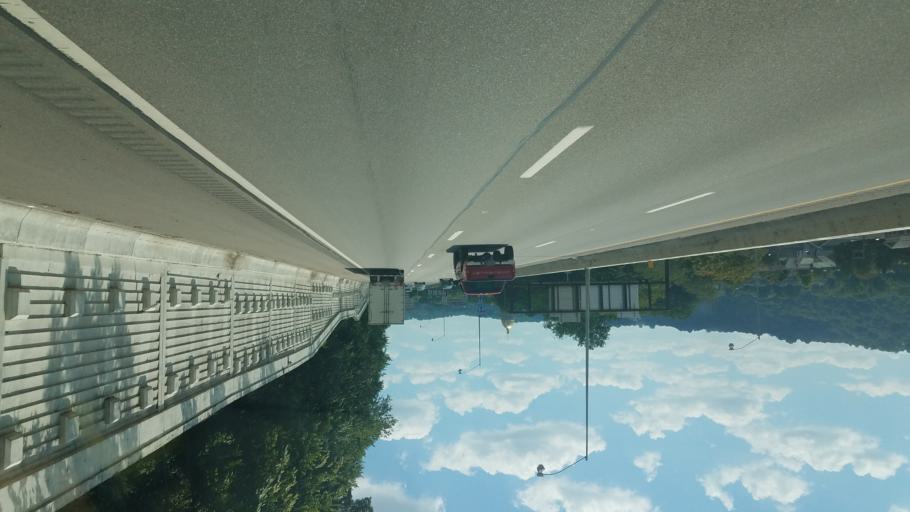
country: US
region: West Virginia
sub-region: Kanawha County
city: Charleston
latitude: 38.3356
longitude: -81.5983
